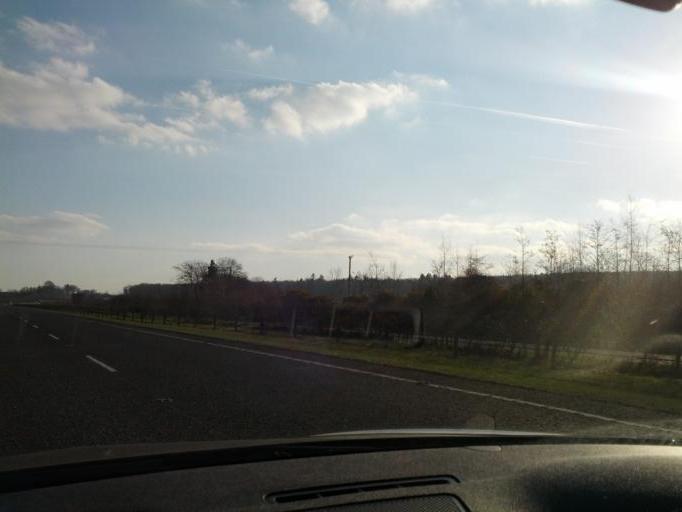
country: IE
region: Leinster
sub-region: Kildare
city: Monasterevin
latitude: 53.1309
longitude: -7.0371
